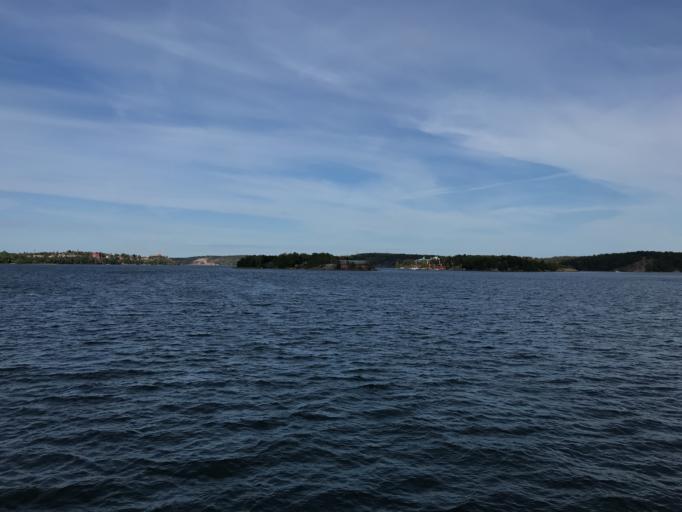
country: SE
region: Stockholm
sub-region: Nacka Kommun
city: Nacka
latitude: 59.3303
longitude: 18.1565
